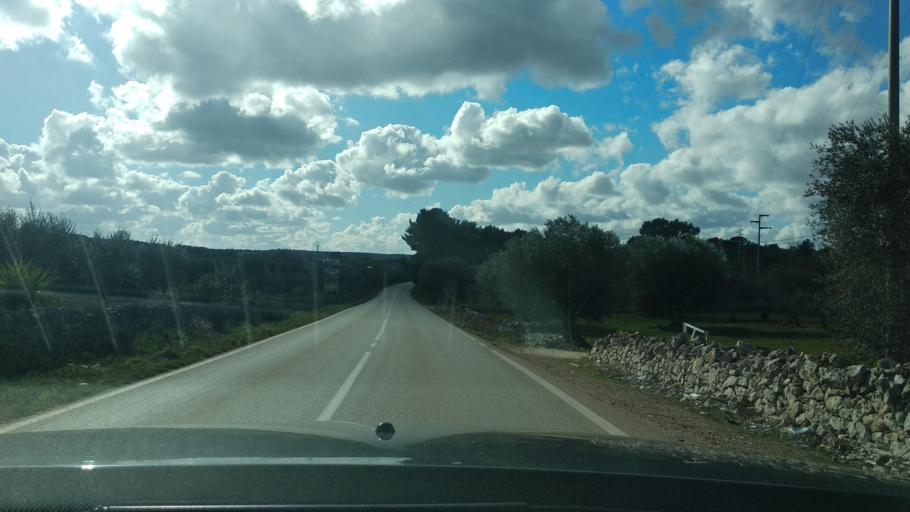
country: IT
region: Apulia
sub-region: Provincia di Brindisi
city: Casalini
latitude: 40.6974
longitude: 17.4840
